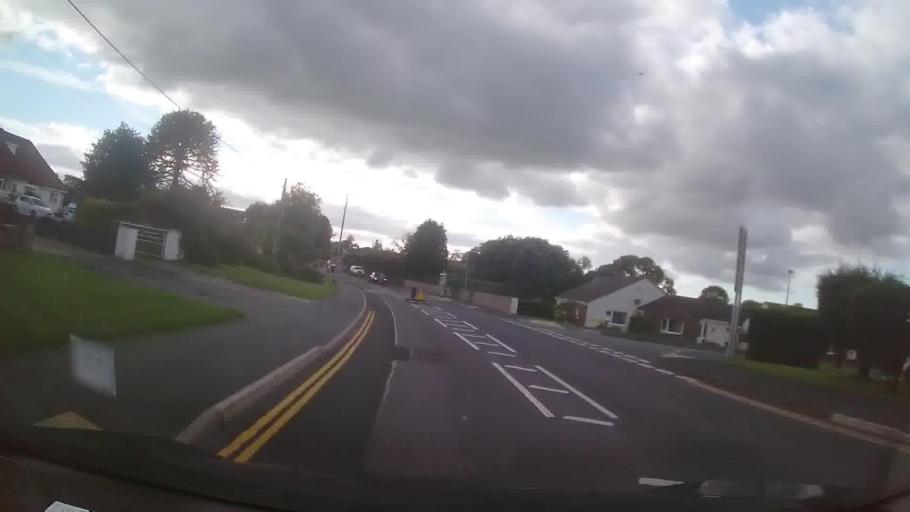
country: GB
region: Wales
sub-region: Pembrokeshire
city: Kilgetty
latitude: 51.7221
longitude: -4.7247
